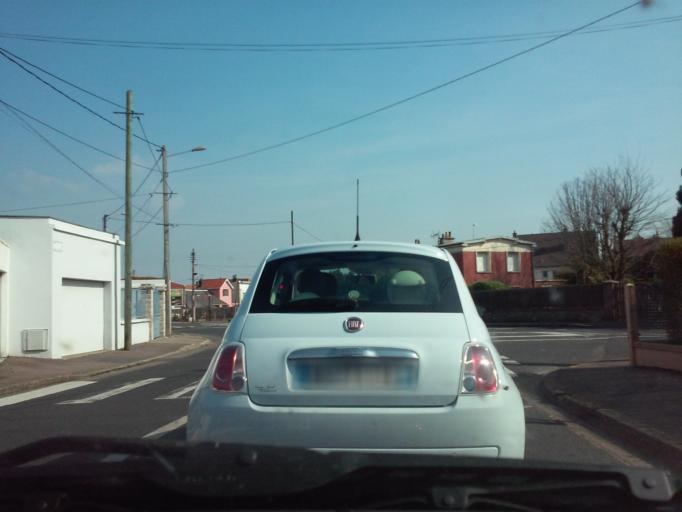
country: FR
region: Haute-Normandie
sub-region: Departement de la Seine-Maritime
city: Le Havre
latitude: 49.5113
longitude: 0.1191
